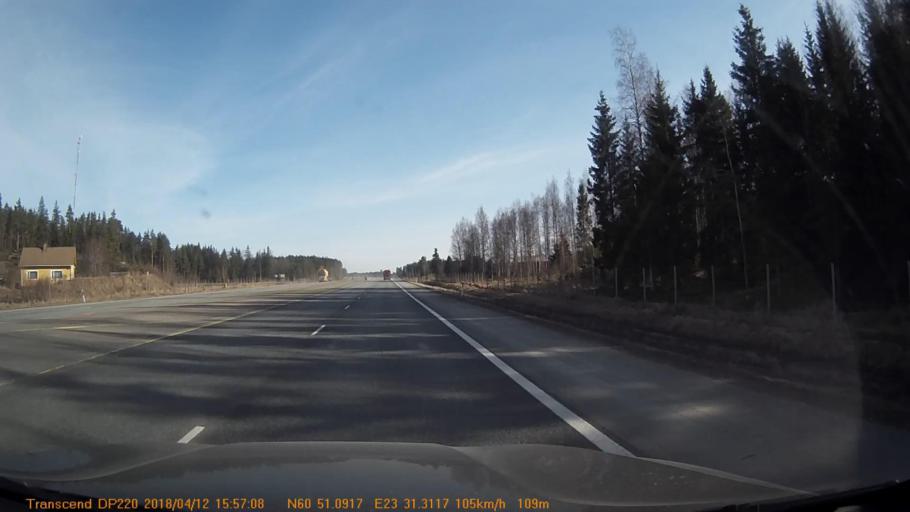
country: FI
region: Haeme
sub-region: Forssa
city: Jokioinen
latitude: 60.8515
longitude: 23.5220
